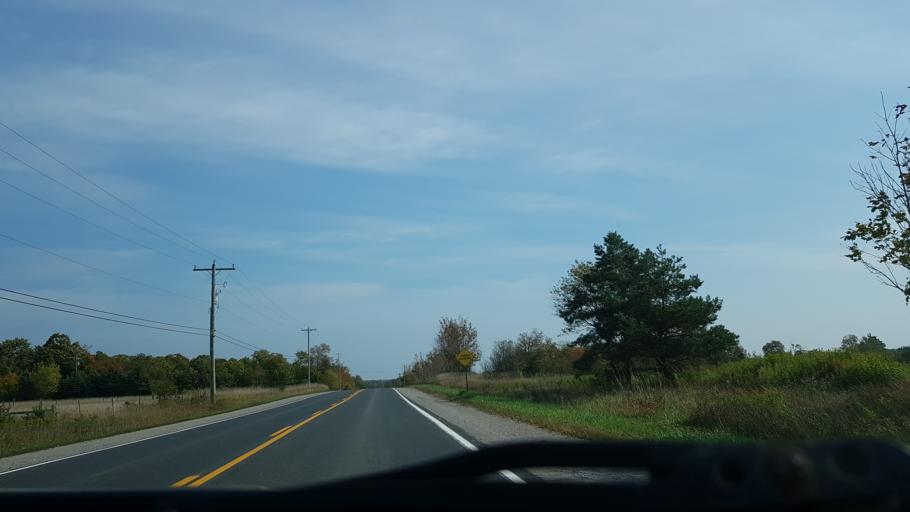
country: CA
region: Ontario
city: Orillia
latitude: 44.6435
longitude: -79.1523
